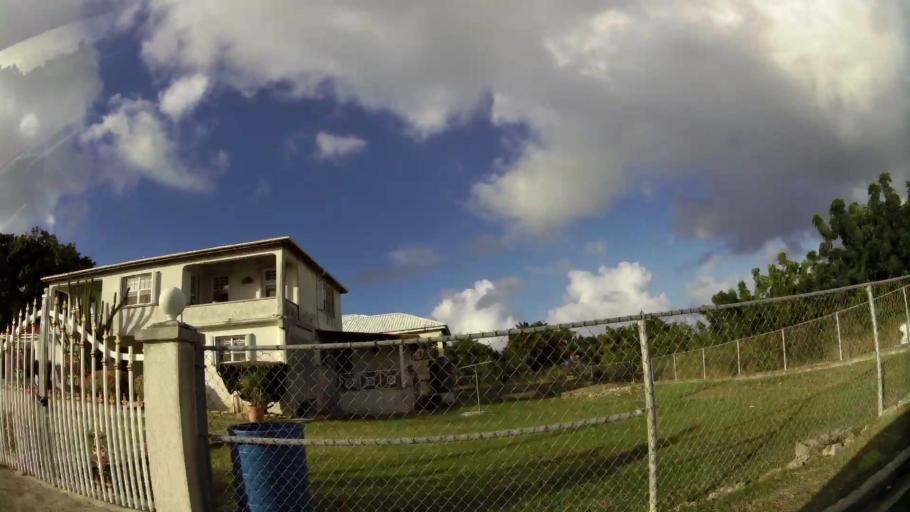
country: AG
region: Saint George
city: Piggotts
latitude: 17.1646
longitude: -61.8149
